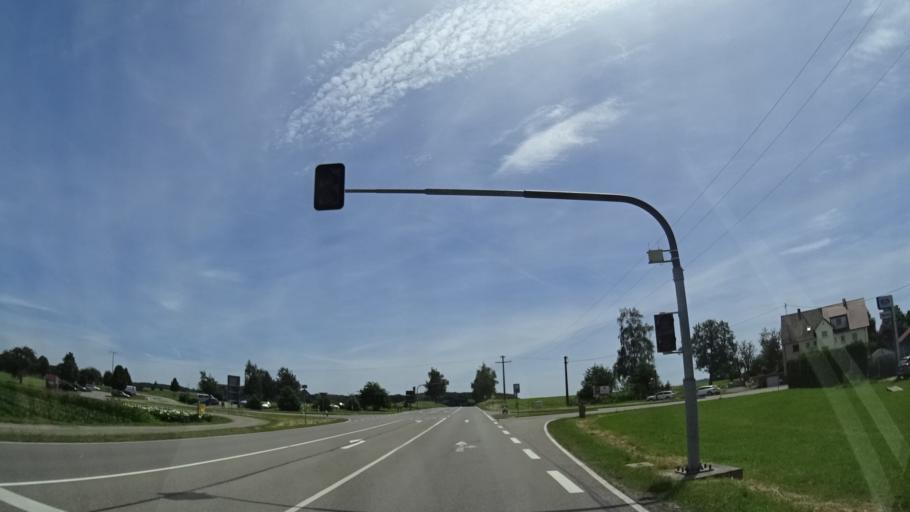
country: DE
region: Baden-Wuerttemberg
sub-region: Regierungsbezirk Stuttgart
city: Kupferzell
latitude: 49.1967
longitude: 9.6899
